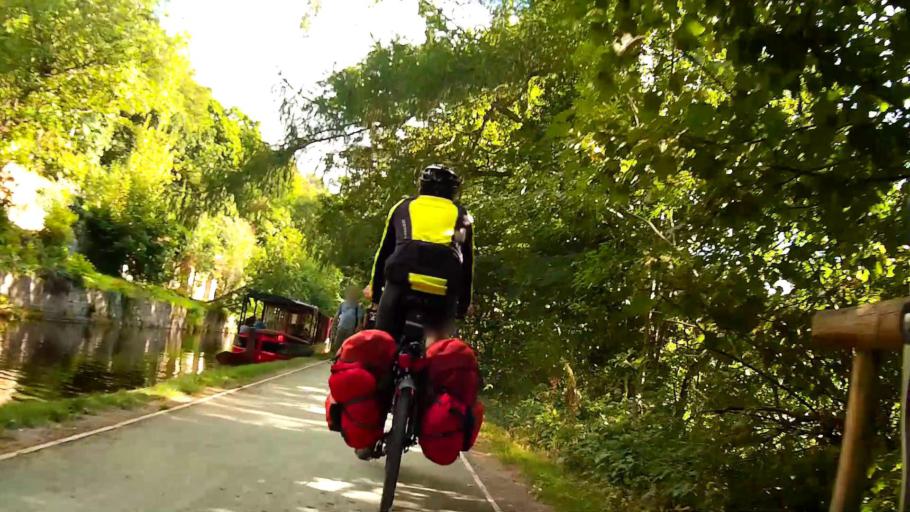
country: GB
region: Wales
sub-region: Denbighshire
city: Llangollen
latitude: 52.9739
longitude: -3.1747
